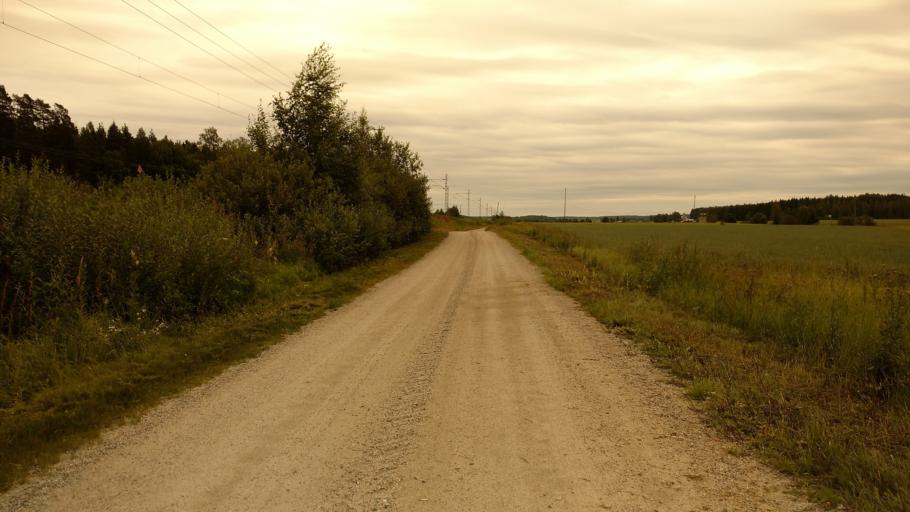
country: FI
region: Varsinais-Suomi
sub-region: Turku
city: Paimio
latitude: 60.4243
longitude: 22.8085
